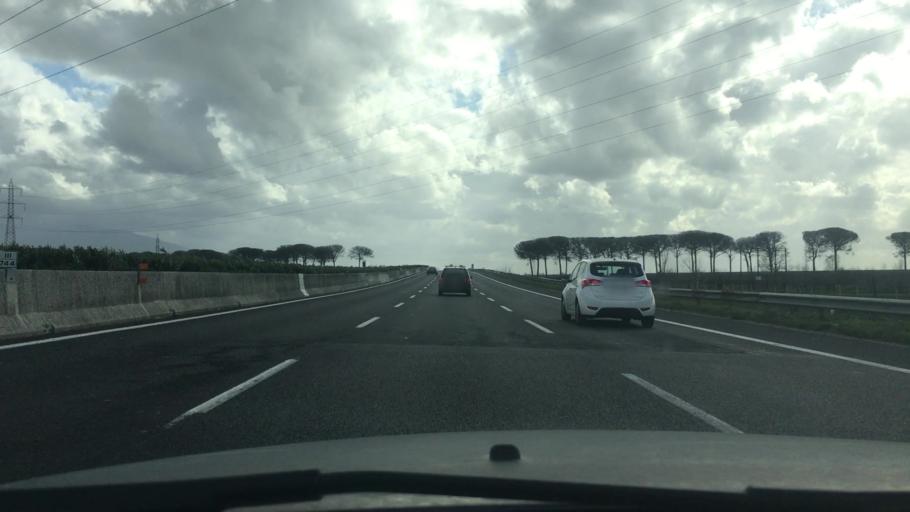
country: IT
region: Campania
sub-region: Provincia di Napoli
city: Pascarola
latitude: 40.9899
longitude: 14.3248
